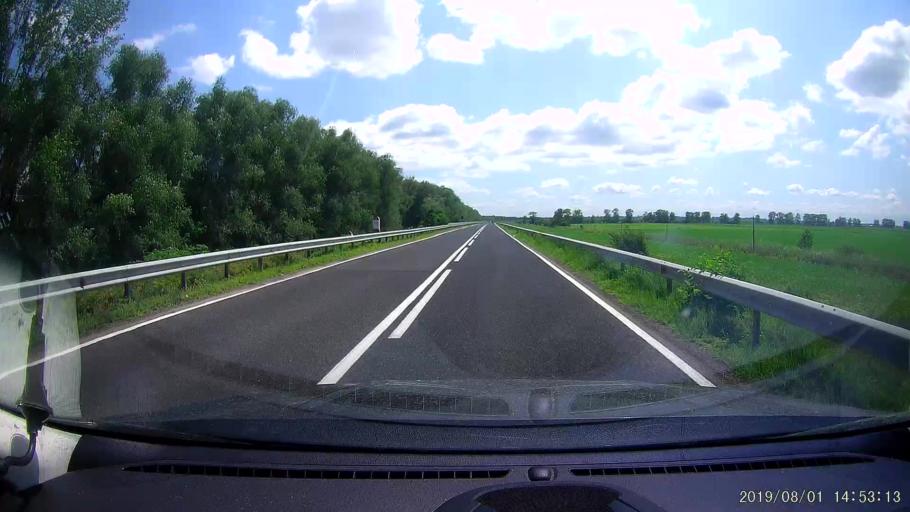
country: RO
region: Braila
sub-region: Comuna Vadeni
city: Vadeni
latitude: 45.3404
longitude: 28.0056
